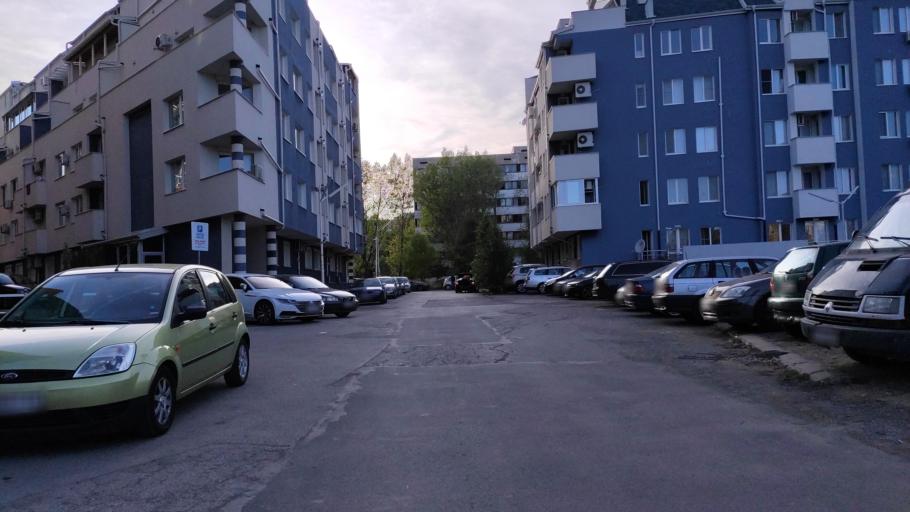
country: BG
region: Sofia-Capital
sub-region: Stolichna Obshtina
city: Sofia
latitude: 42.6549
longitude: 23.3463
